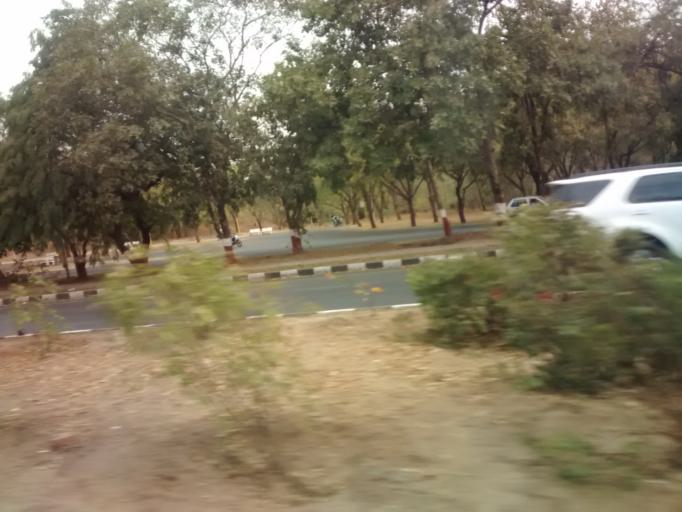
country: IN
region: Gujarat
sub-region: Gandhinagar
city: Ghandinagar
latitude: 23.2237
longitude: 72.6549
